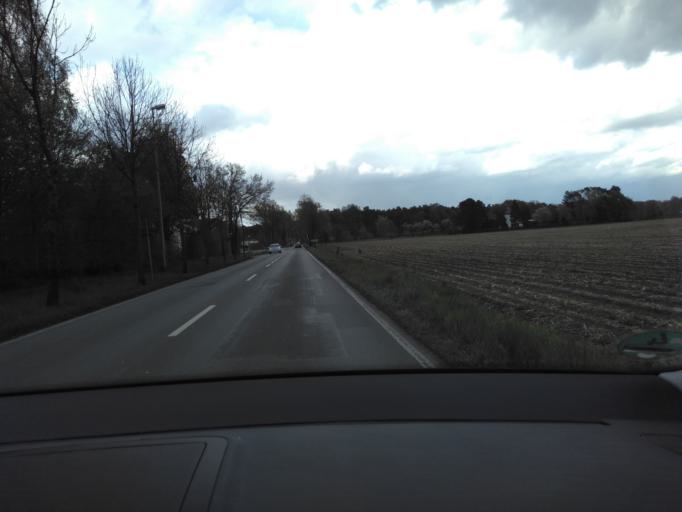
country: DE
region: North Rhine-Westphalia
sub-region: Regierungsbezirk Detmold
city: Verl
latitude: 51.8825
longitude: 8.4551
